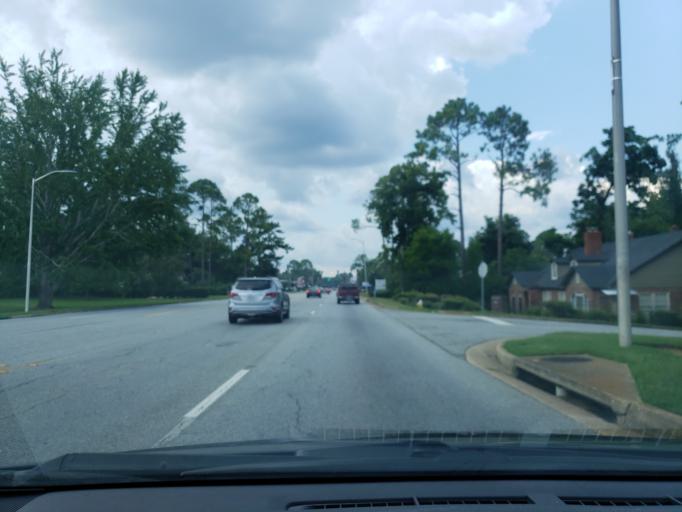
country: US
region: Georgia
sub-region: Dougherty County
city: Albany
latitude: 31.5857
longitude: -84.1825
